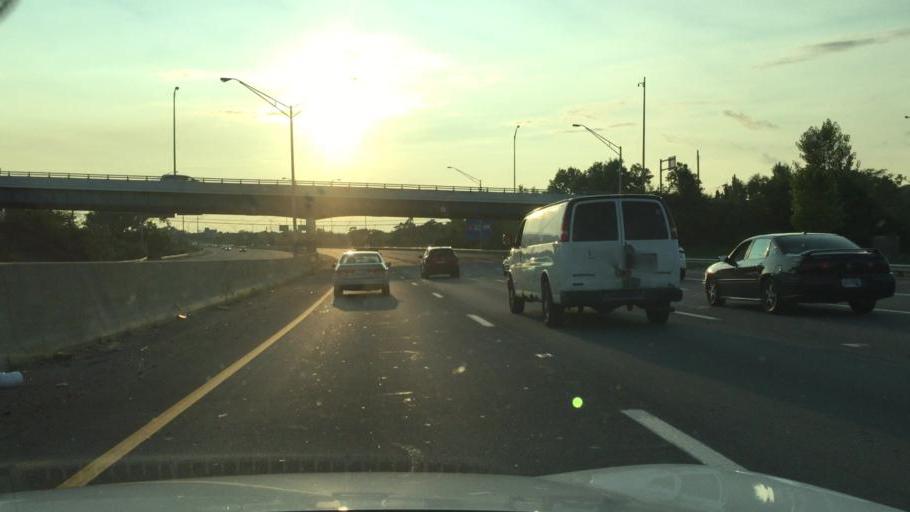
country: US
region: Ohio
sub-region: Franklin County
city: Grandview Heights
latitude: 39.9697
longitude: -83.0458
